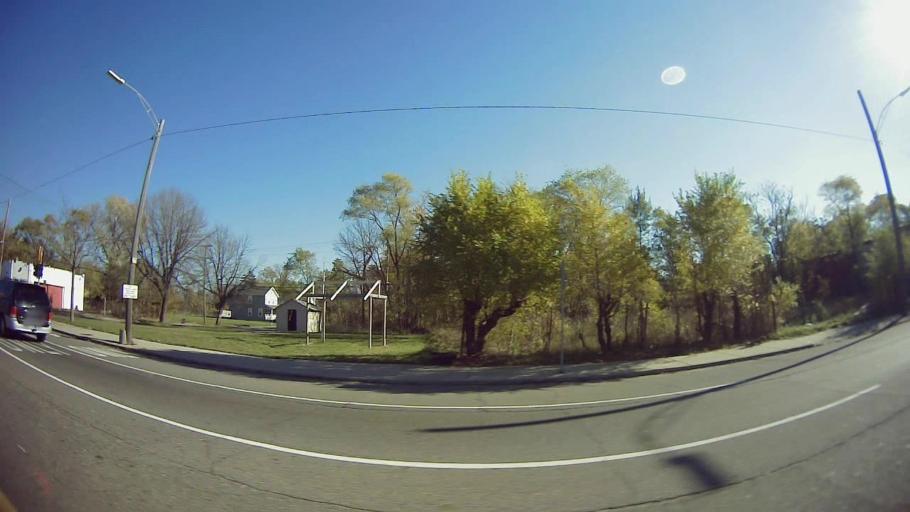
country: US
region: Michigan
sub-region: Wayne County
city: Highland Park
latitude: 42.3995
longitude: -83.1594
